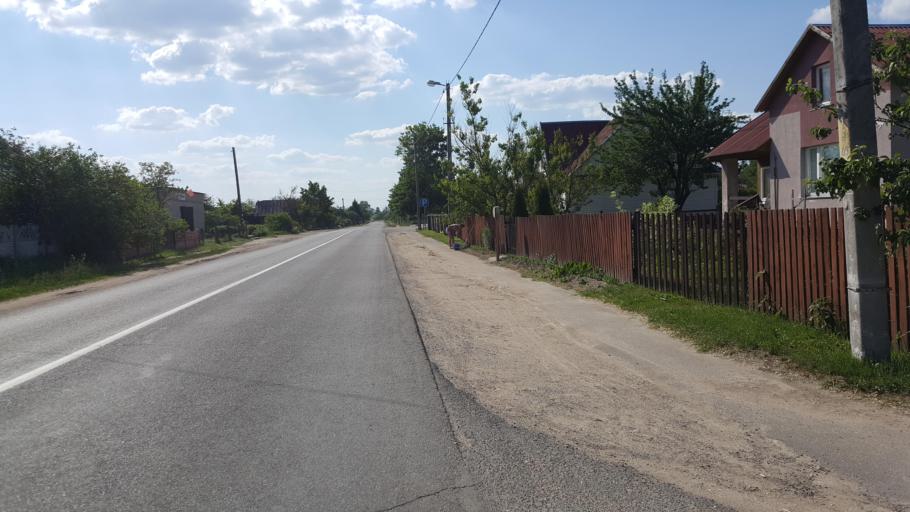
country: BY
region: Brest
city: Kobryn
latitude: 52.3377
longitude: 24.2493
